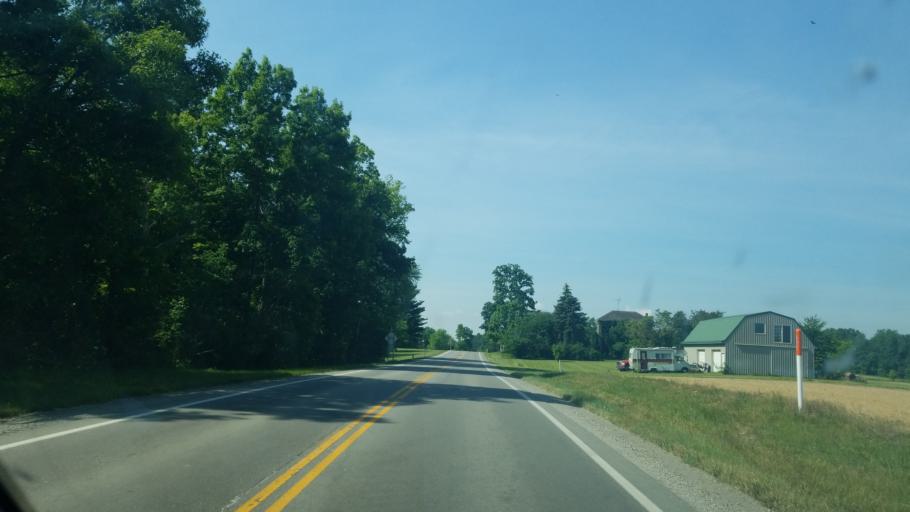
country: US
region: Ohio
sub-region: Wyandot County
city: Carey
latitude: 40.9740
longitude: -83.2720
